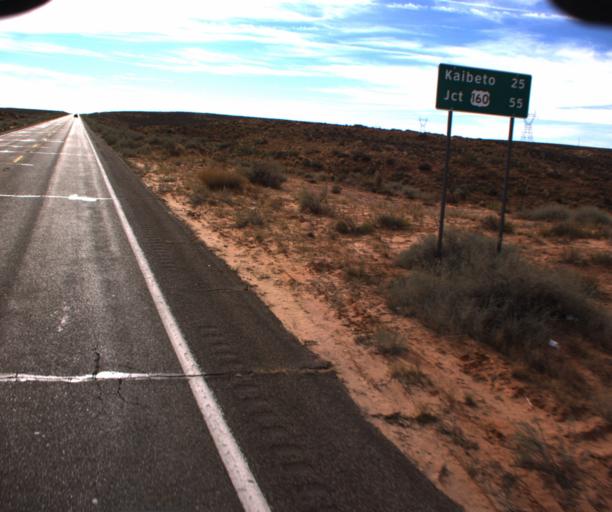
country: US
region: Arizona
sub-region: Coconino County
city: LeChee
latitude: 36.8392
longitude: -111.3236
